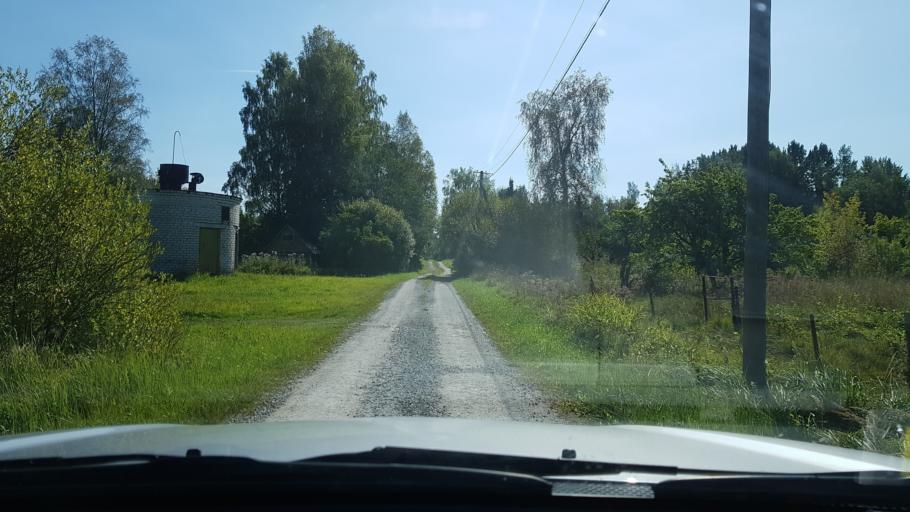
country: EE
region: Ida-Virumaa
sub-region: Sillamaee linn
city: Sillamae
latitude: 59.3189
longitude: 27.7829
